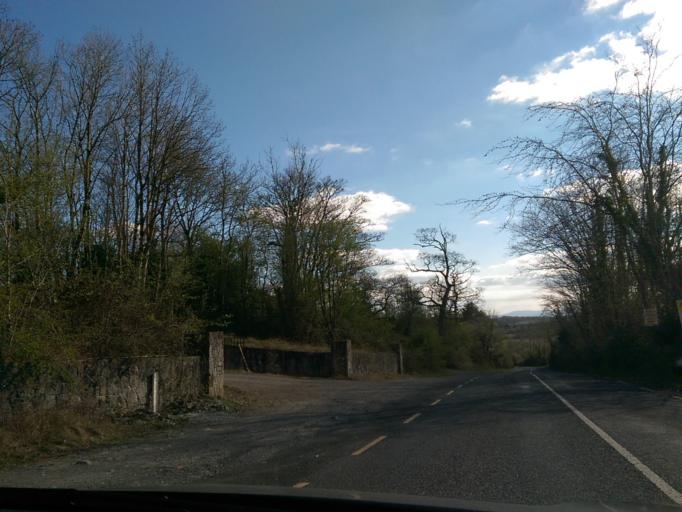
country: IE
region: Connaught
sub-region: County Galway
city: Portumna
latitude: 53.0971
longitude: -8.1811
